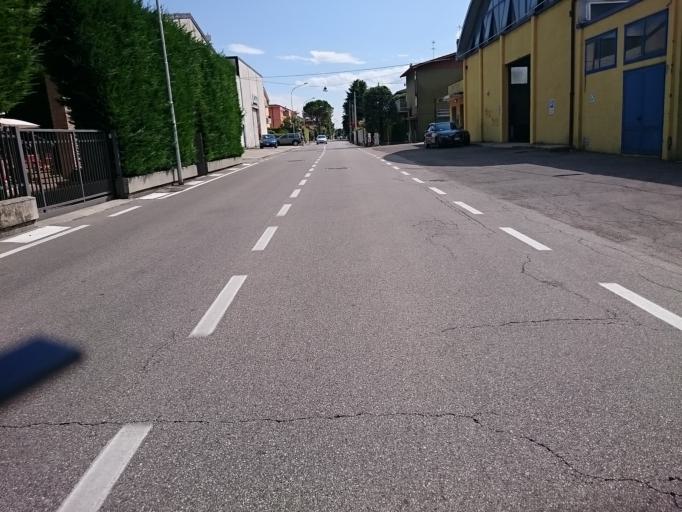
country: IT
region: Veneto
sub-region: Provincia di Padova
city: Caselle
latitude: 45.4172
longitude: 11.8096
